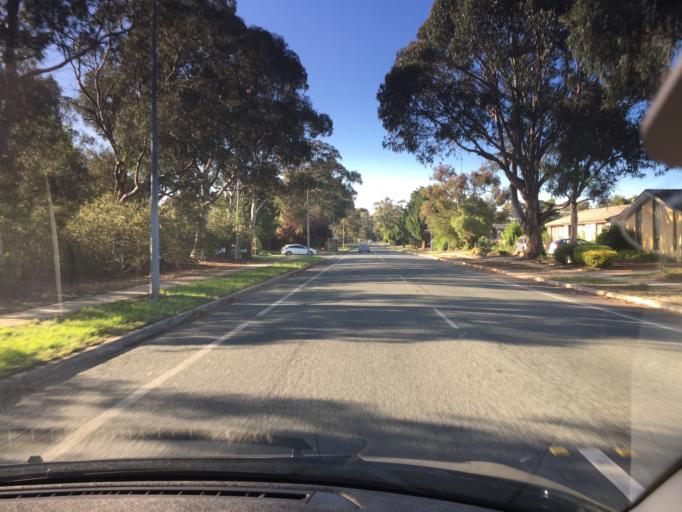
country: AU
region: Australian Capital Territory
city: Kaleen
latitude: -35.2259
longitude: 149.1111
